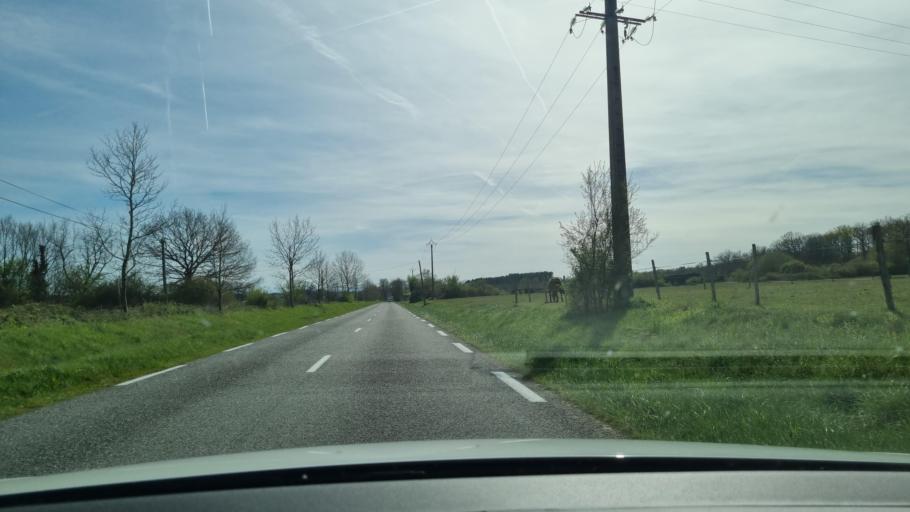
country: FR
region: Midi-Pyrenees
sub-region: Departement du Gers
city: Lombez
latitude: 43.4101
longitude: 0.8028
